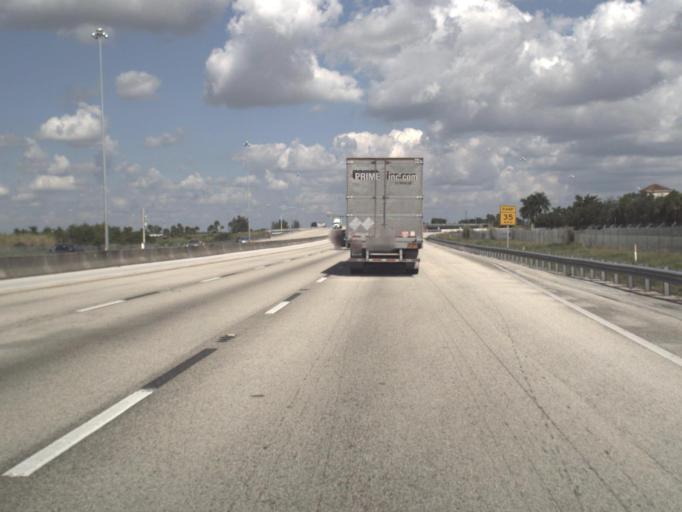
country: US
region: Florida
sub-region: Palm Beach County
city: Villages of Oriole
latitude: 26.5216
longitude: -80.1725
